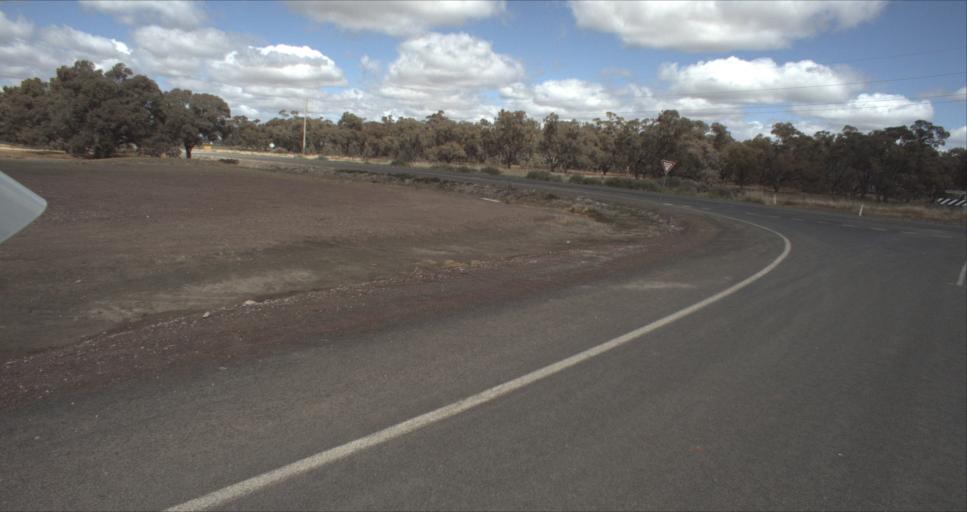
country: AU
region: New South Wales
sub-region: Murrumbidgee Shire
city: Darlington Point
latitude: -34.5746
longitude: 146.1669
